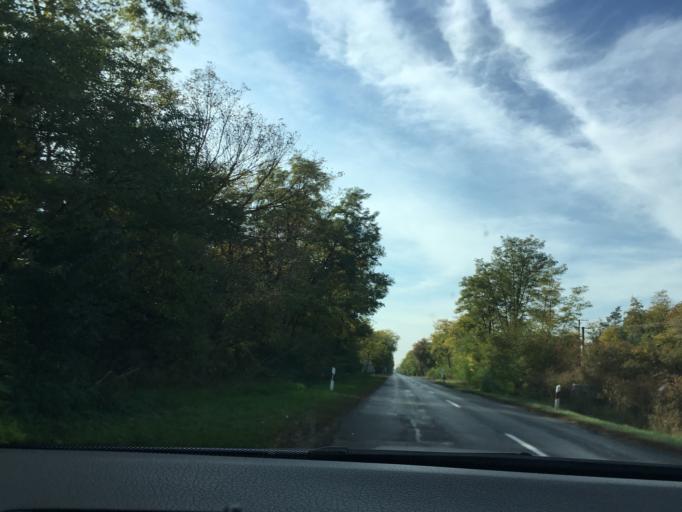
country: HU
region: Hajdu-Bihar
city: Hajdusamson
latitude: 47.5275
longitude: 21.8010
